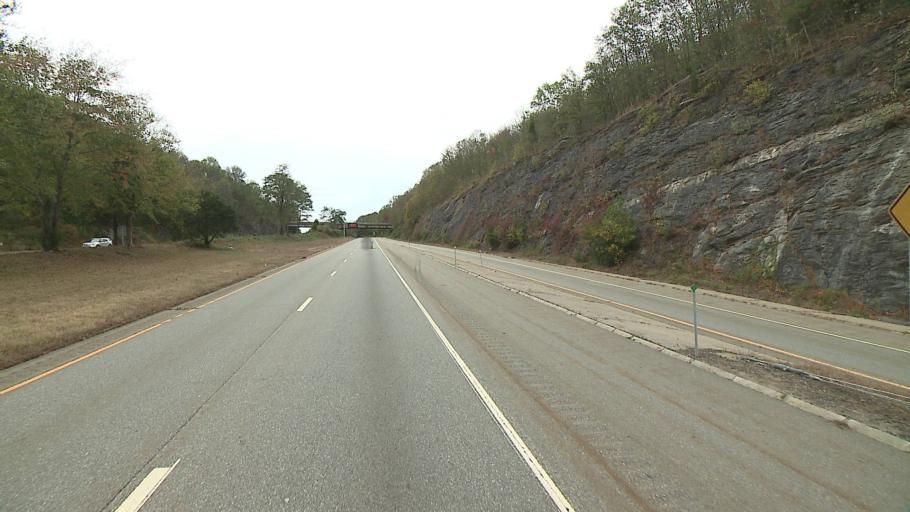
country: US
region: Connecticut
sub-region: Middlesex County
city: Chester Center
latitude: 41.4038
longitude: -72.4744
